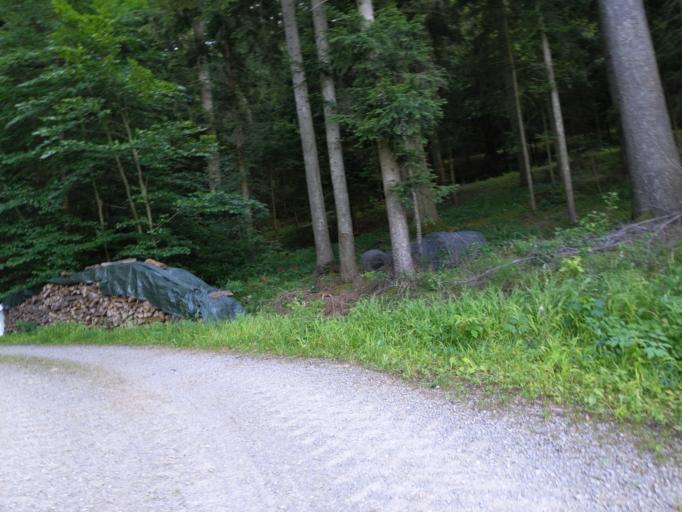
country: DE
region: Baden-Wuerttemberg
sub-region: Karlsruhe Region
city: Glatten
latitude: 48.3990
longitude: 8.5048
